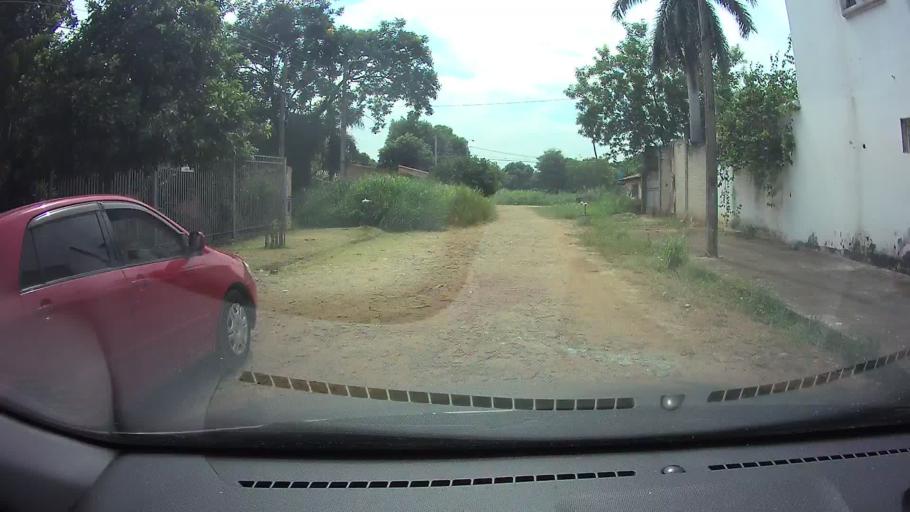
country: PY
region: Central
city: San Lorenzo
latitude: -25.2906
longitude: -57.5070
